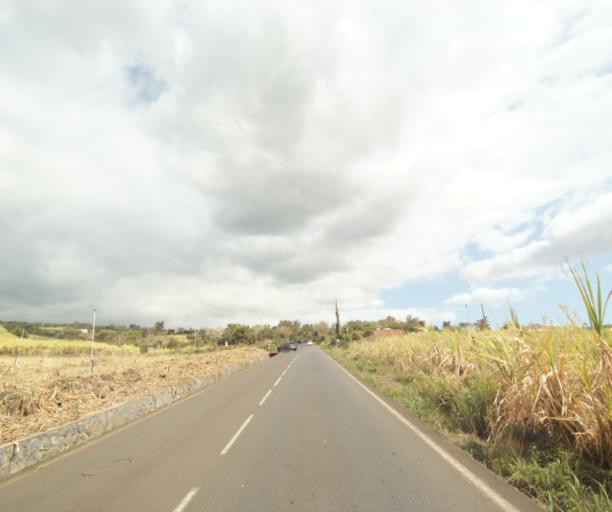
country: RE
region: Reunion
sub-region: Reunion
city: Saint-Paul
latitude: -21.0329
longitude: 55.2863
